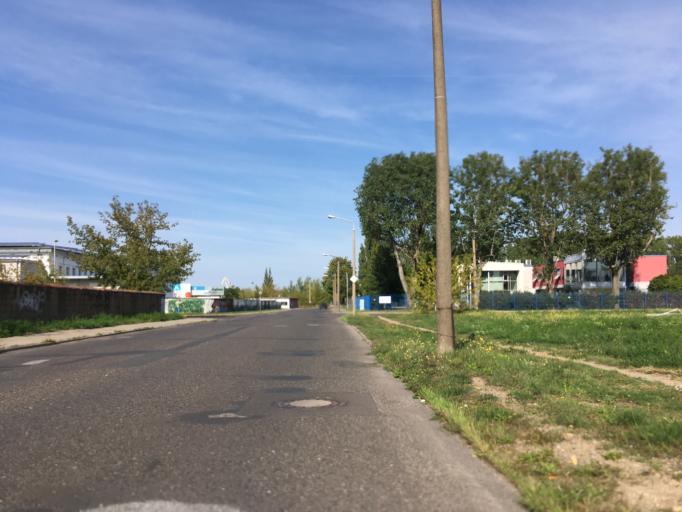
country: DE
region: Brandenburg
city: Eisenhuettenstadt
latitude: 52.1449
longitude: 14.6504
